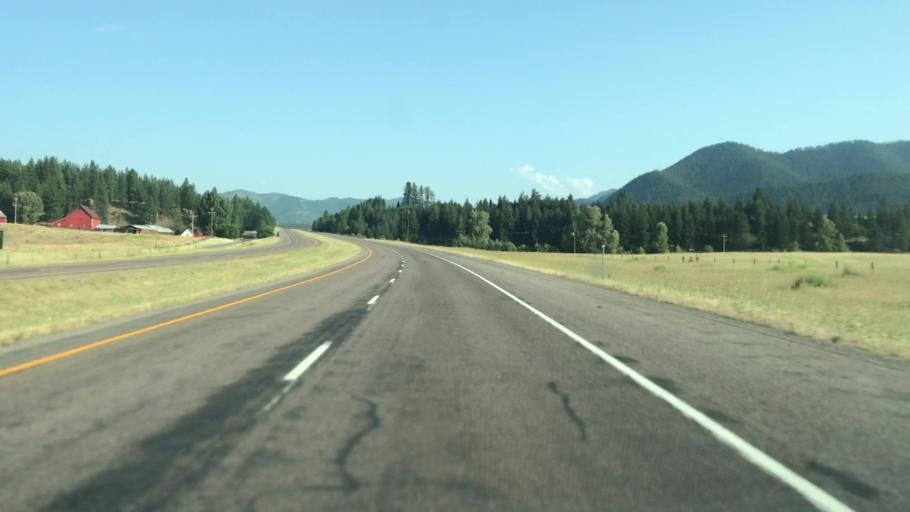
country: US
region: Montana
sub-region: Mineral County
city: Superior
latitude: 47.0575
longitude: -114.7621
